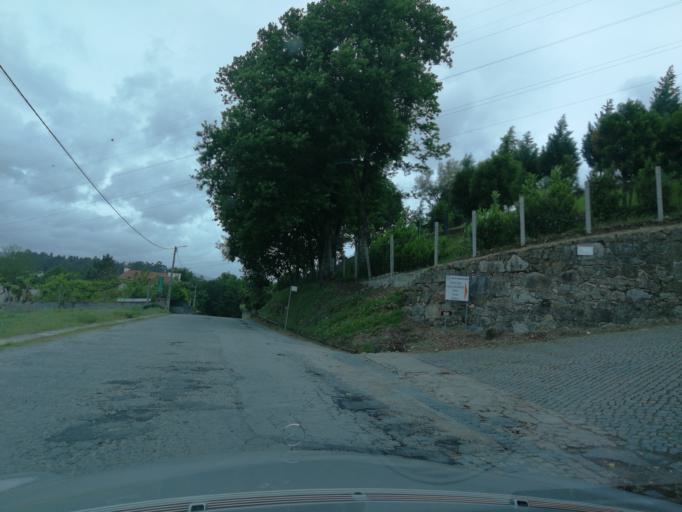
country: PT
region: Braga
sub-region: Braga
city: Adaufe
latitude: 41.6029
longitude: -8.4083
